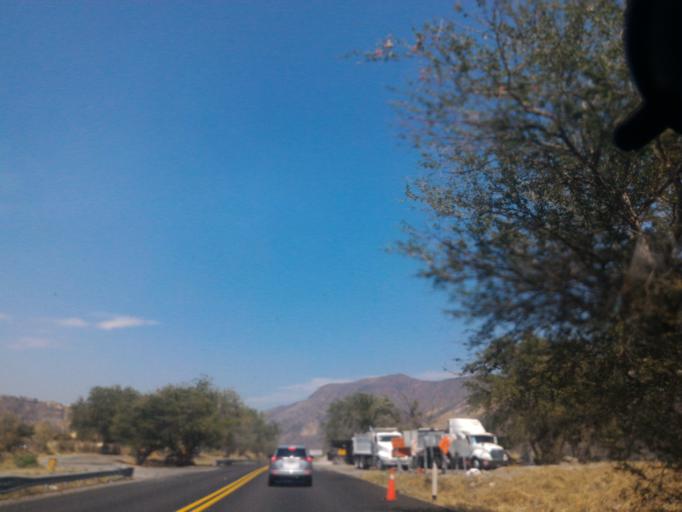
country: MX
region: Jalisco
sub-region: Tonila
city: San Marcos
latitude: 19.4776
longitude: -103.4587
